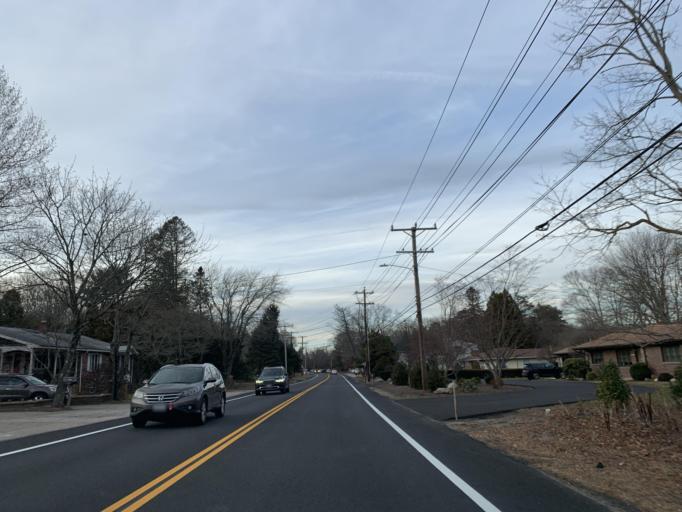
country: US
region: Rhode Island
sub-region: Providence County
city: Greenville
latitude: 41.8571
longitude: -71.5265
